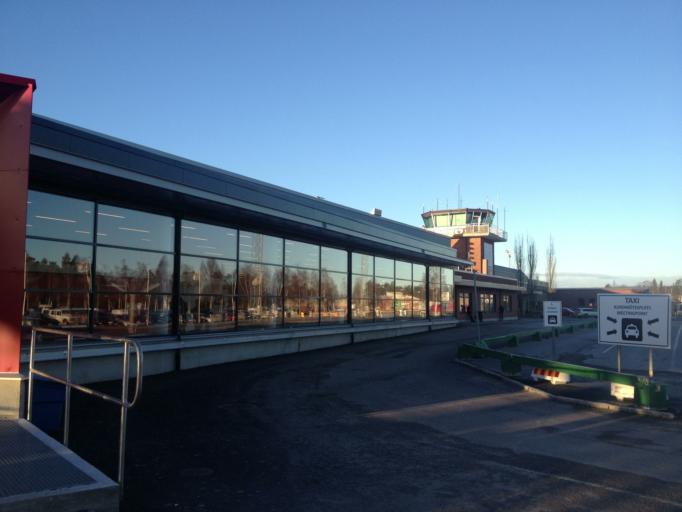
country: SE
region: Vaesterbotten
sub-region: Umea Kommun
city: Umea
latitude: 63.7930
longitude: 20.2904
